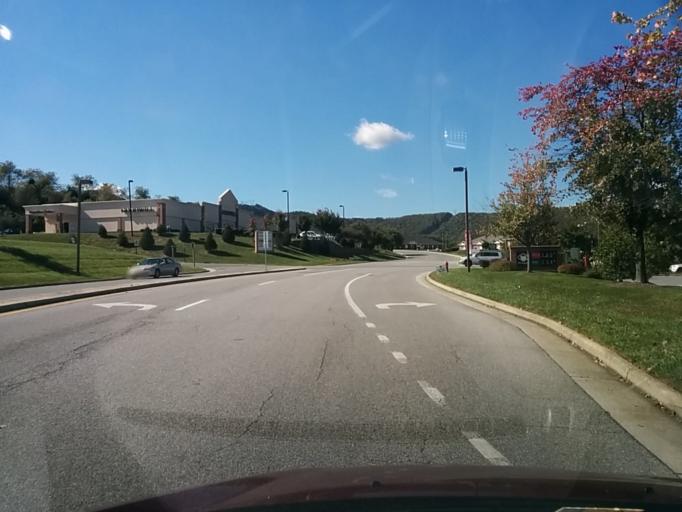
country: US
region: Virginia
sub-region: Botetourt County
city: Daleville
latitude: 37.3961
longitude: -79.9090
